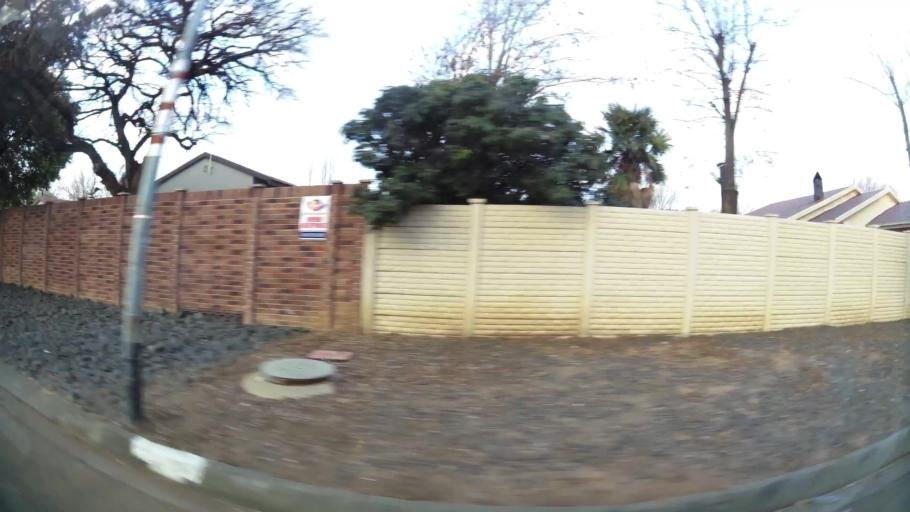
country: ZA
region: Orange Free State
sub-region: Mangaung Metropolitan Municipality
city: Bloemfontein
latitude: -29.1370
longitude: 26.1755
